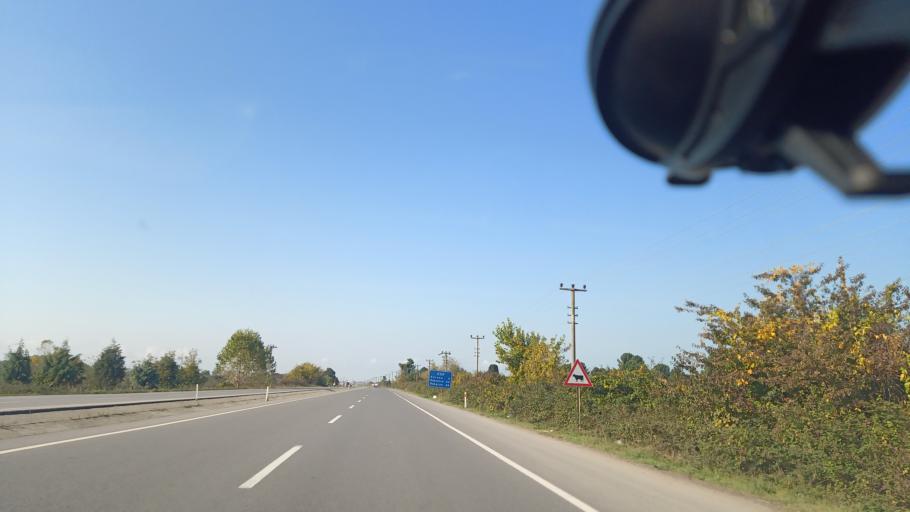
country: TR
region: Sakarya
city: Karasu
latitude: 41.0767
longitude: 30.7792
